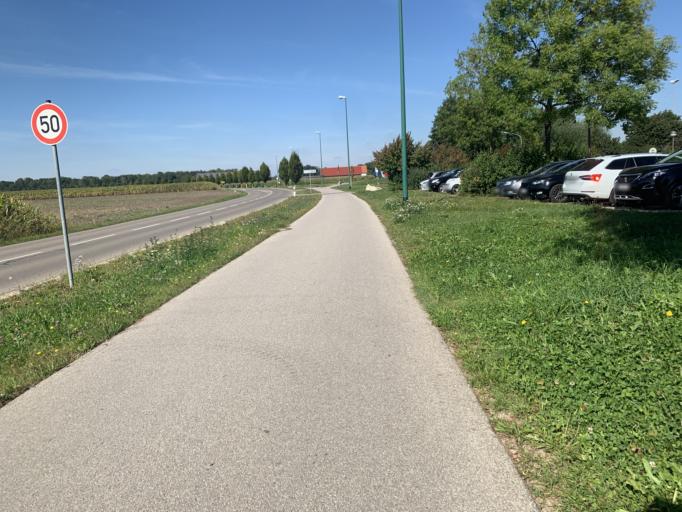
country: DE
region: Bavaria
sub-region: Swabia
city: Kissing
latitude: 48.3060
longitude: 10.9805
